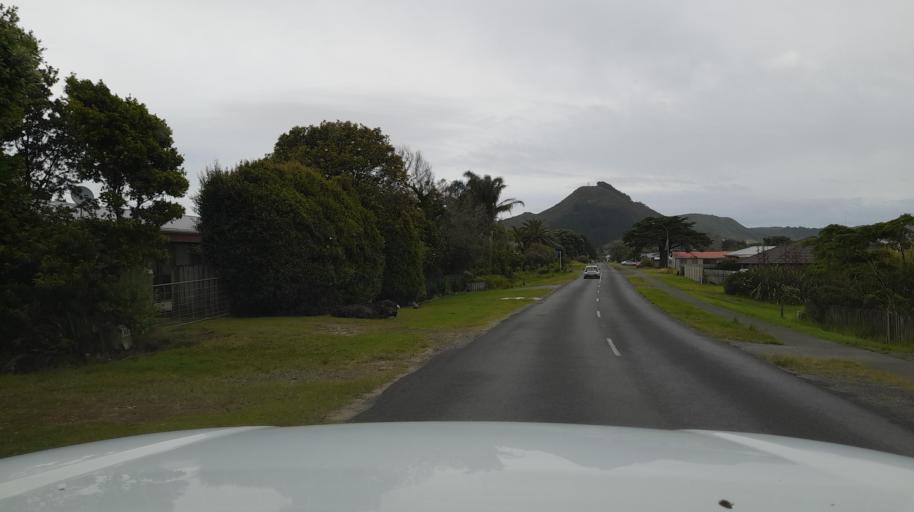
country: NZ
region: Northland
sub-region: Far North District
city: Ahipara
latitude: -35.1624
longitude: 173.1588
